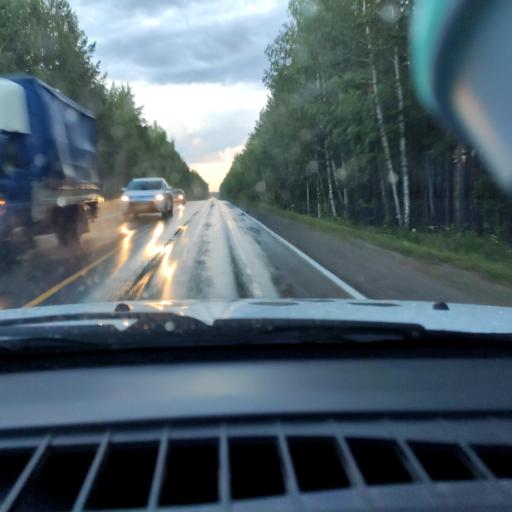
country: RU
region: Chelyabinsk
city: Ozersk
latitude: 55.8135
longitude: 60.6376
